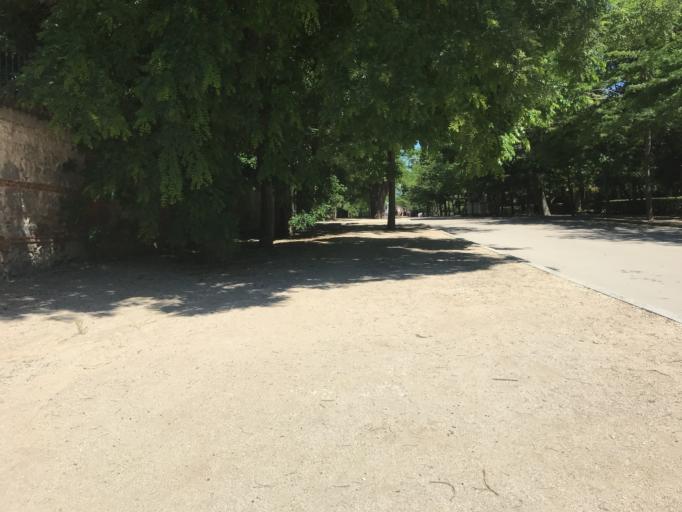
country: ES
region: Madrid
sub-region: Provincia de Madrid
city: Retiro
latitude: 40.4097
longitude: -3.6821
